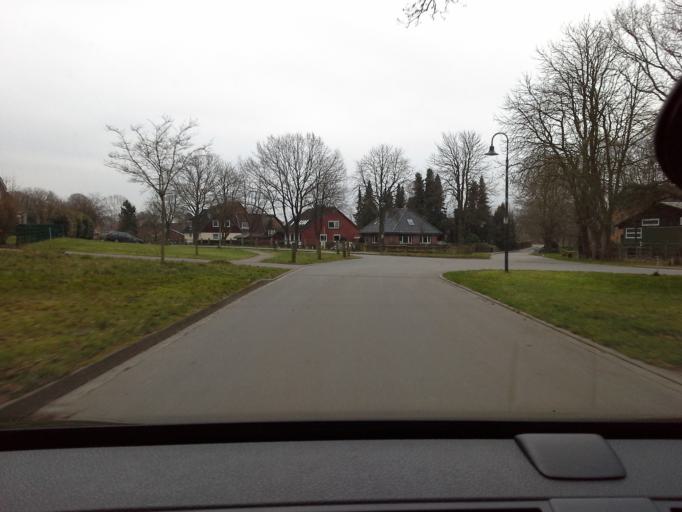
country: DE
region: Schleswig-Holstein
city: Lentfohrden
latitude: 53.8743
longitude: 9.8796
